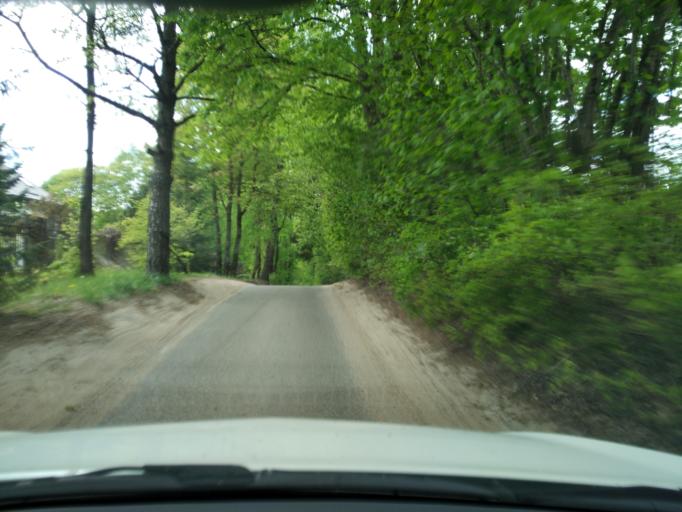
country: LT
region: Vilnius County
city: Rasos
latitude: 54.6949
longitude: 25.3284
